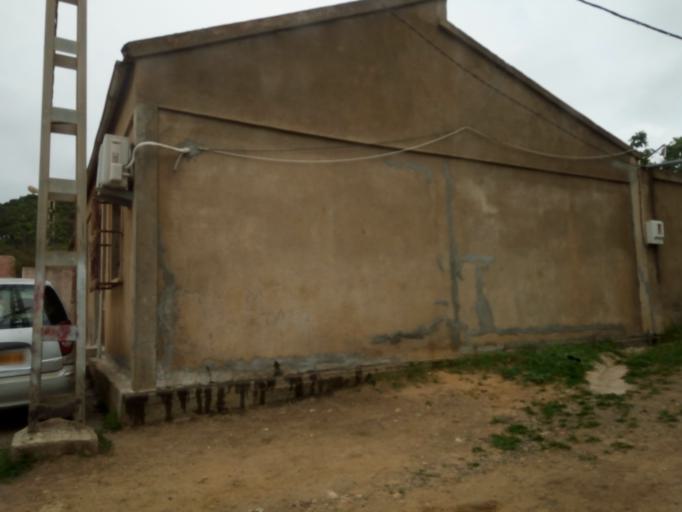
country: DZ
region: Tipaza
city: Tipasa
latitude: 36.5888
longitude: 2.4983
